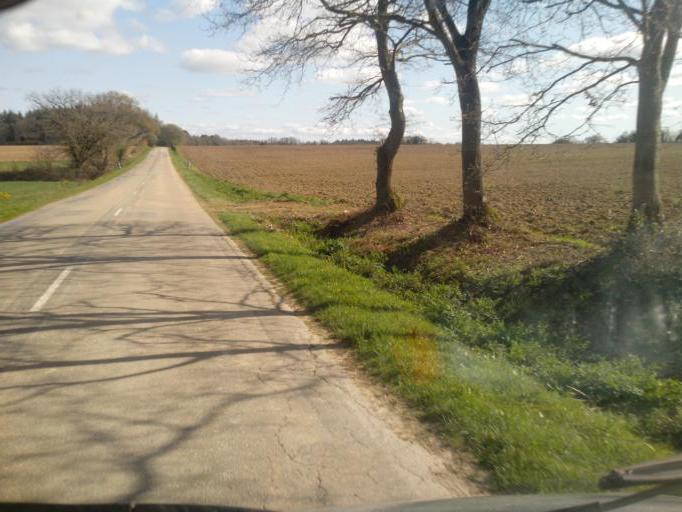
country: FR
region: Brittany
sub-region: Departement d'Ille-et-Vilaine
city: Maxent
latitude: 47.9525
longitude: -2.0111
